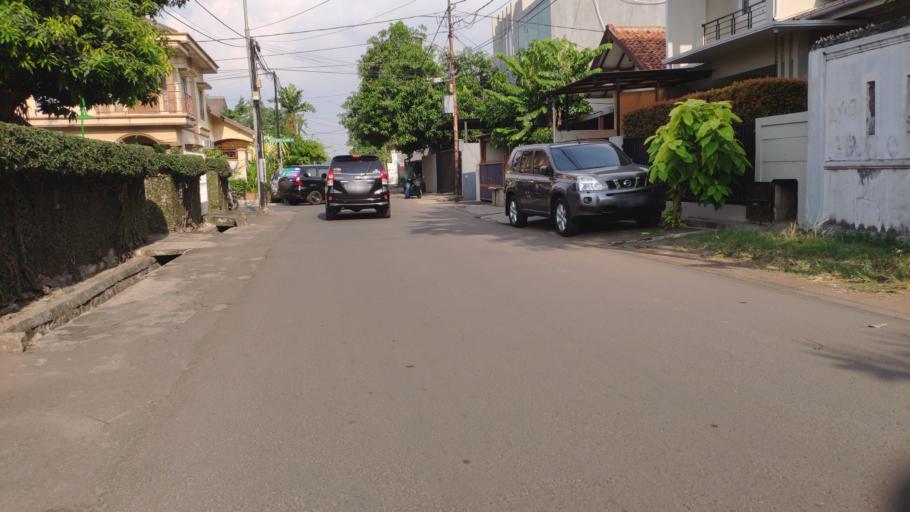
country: ID
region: West Java
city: Pamulang
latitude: -6.3024
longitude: 106.8018
